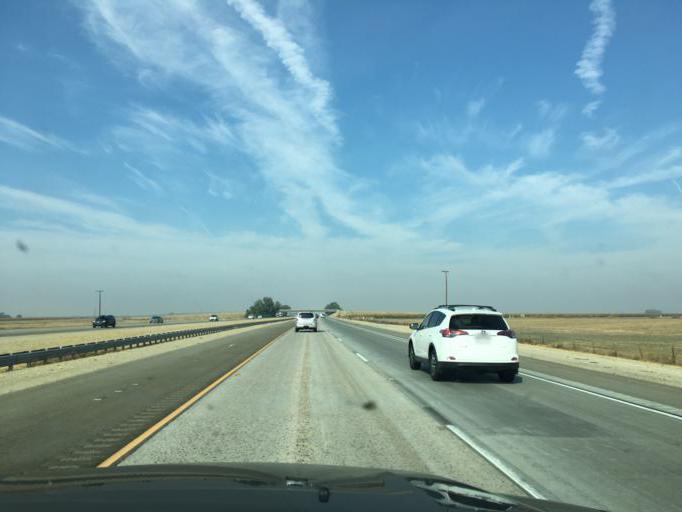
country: US
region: California
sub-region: Kern County
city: Lost Hills
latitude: 35.5711
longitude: -119.6120
